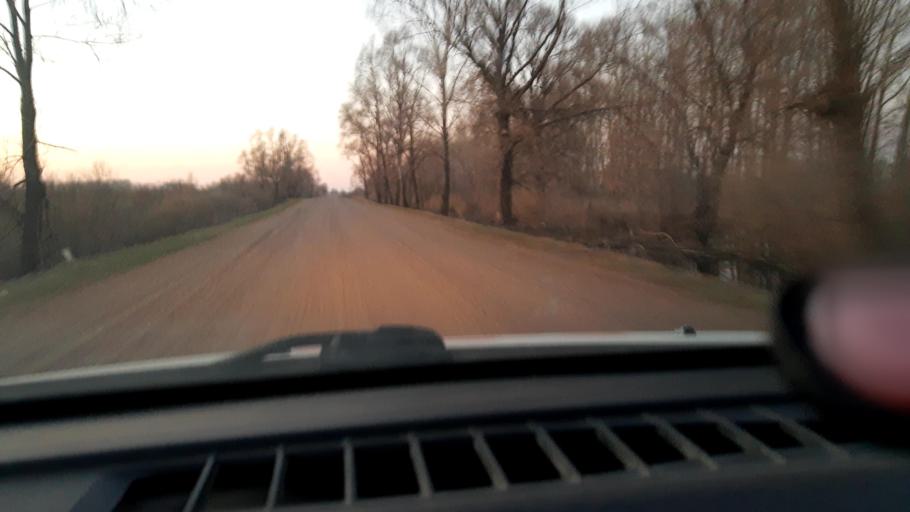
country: RU
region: Bashkortostan
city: Asanovo
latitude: 54.8620
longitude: 55.4619
